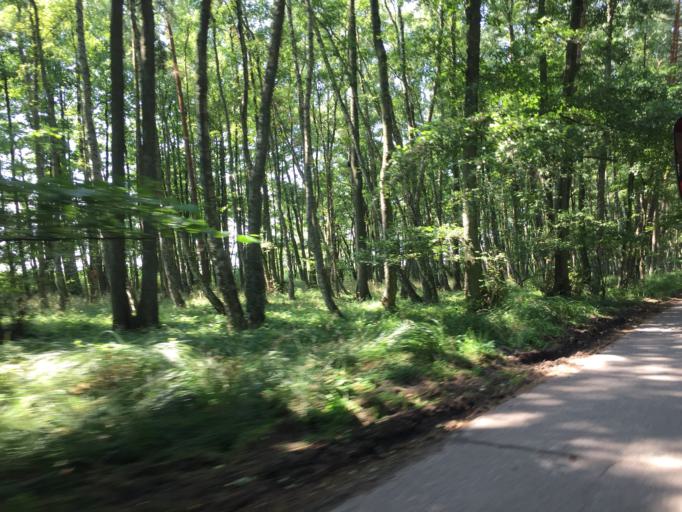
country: PL
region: Pomeranian Voivodeship
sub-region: Powiat leborski
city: Leba
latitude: 54.7524
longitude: 17.4850
